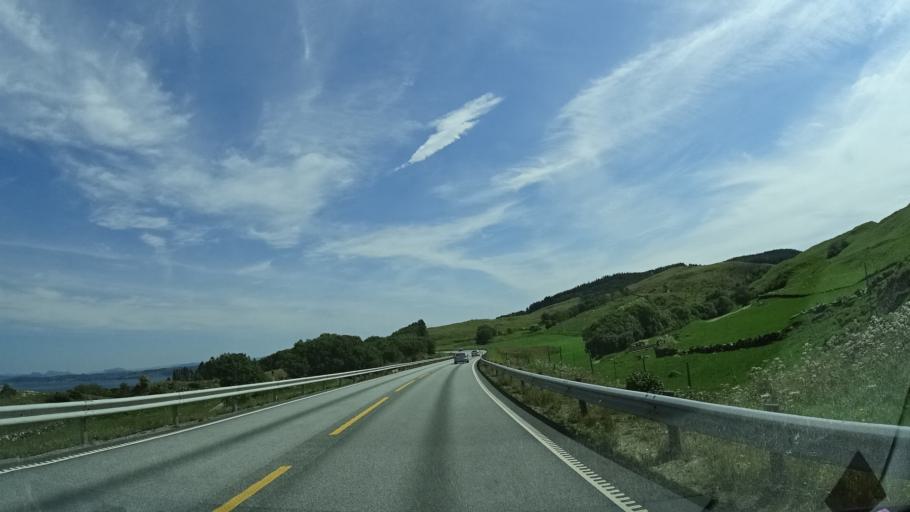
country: NO
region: Rogaland
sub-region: Rennesoy
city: Vikevag
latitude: 59.1264
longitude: 5.6463
